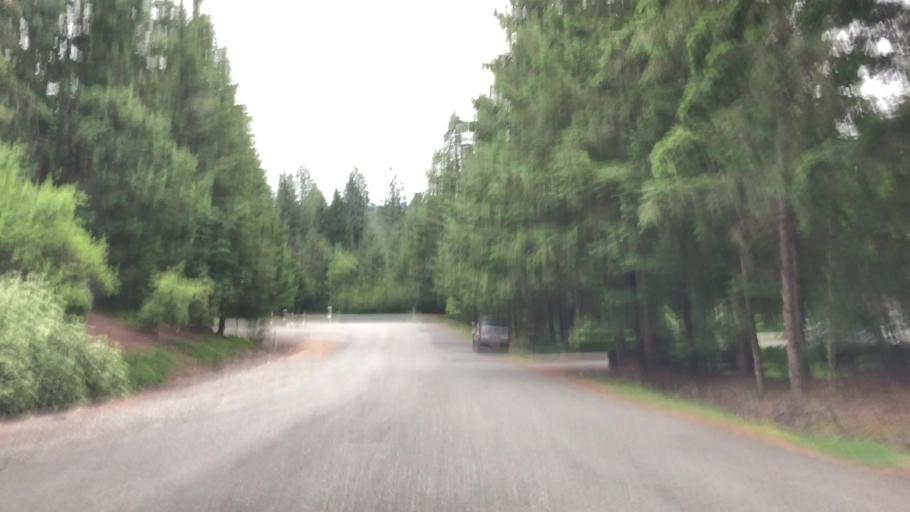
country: US
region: Washington
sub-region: King County
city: Cottage Lake
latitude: 47.7185
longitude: -122.0925
